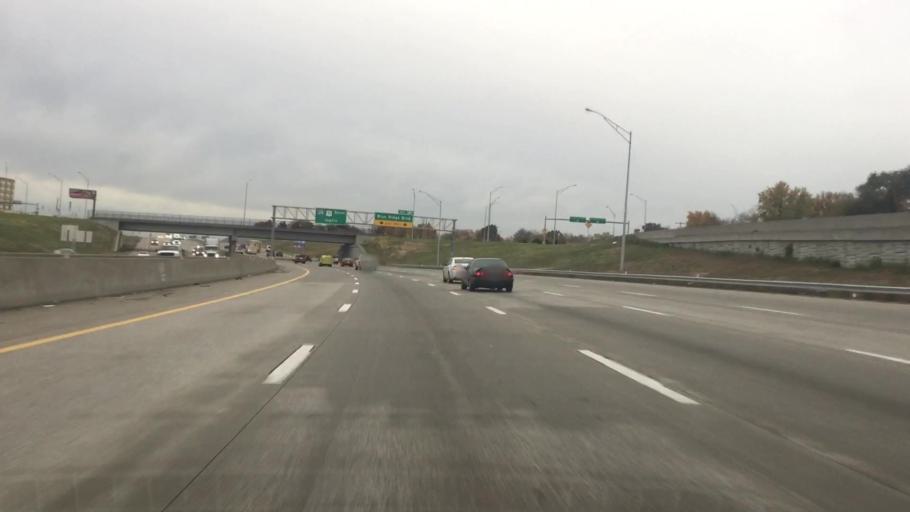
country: US
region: Missouri
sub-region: Jackson County
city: Grandview
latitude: 38.9185
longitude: -94.5278
